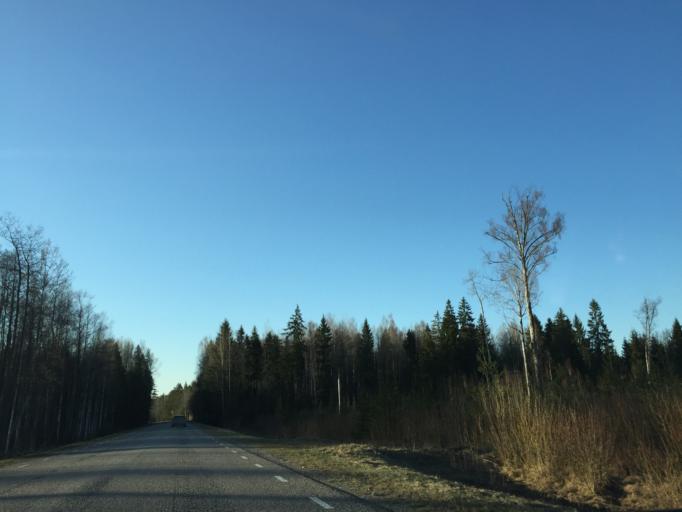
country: EE
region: Ida-Virumaa
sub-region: Toila vald
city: Voka
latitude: 59.1511
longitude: 27.6073
